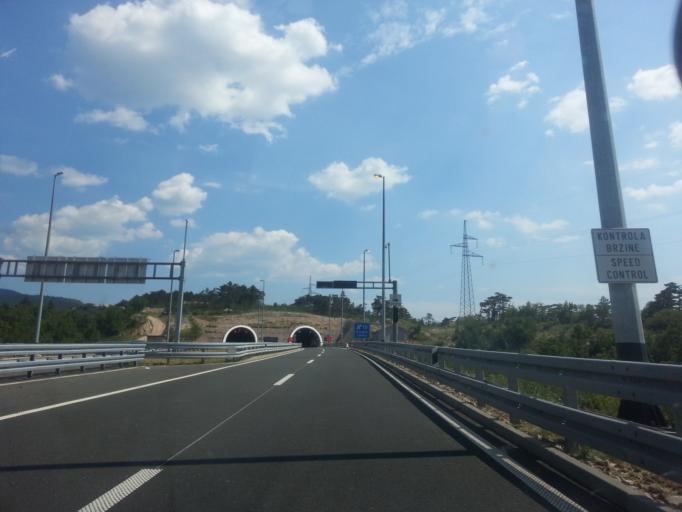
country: HR
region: Primorsko-Goranska
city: Hreljin
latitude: 45.2858
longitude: 14.5874
